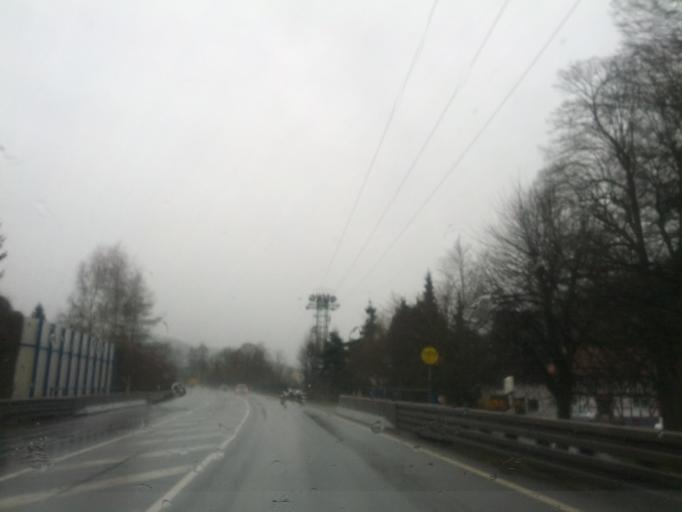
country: DE
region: Hesse
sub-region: Regierungsbezirk Kassel
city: Sontra
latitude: 51.1105
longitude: 9.9692
